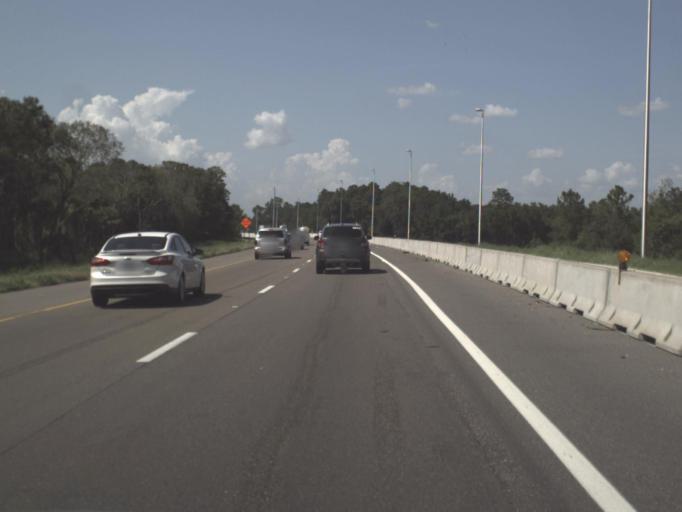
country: US
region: Florida
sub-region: Hillsborough County
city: Thonotosassa
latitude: 28.0843
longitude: -82.3532
